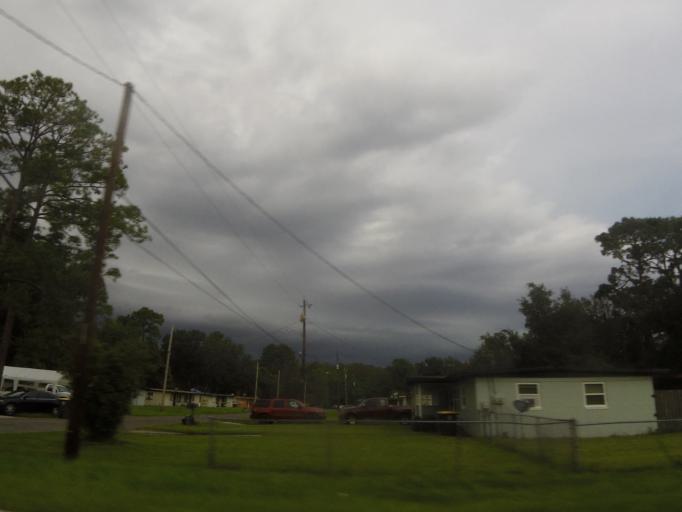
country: US
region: Florida
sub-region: Clay County
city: Bellair-Meadowbrook Terrace
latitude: 30.2843
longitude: -81.7934
